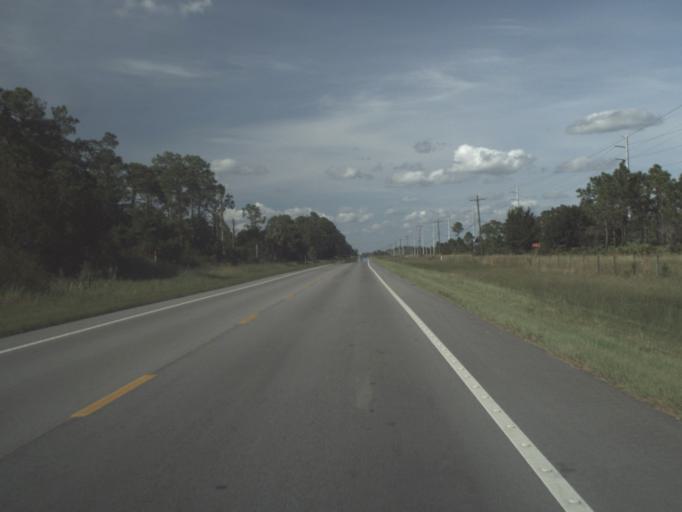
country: US
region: Florida
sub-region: Lee County
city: Fort Myers Shores
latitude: 26.8192
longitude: -81.7601
